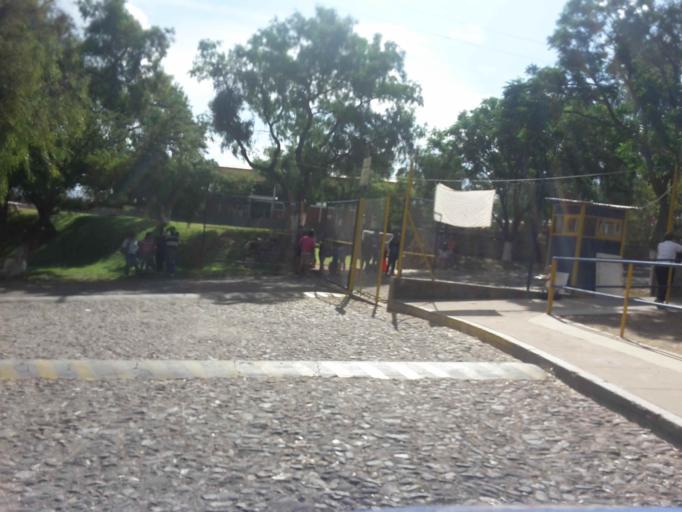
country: BO
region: Cochabamba
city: Cochabamba
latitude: -17.3711
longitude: -66.1318
